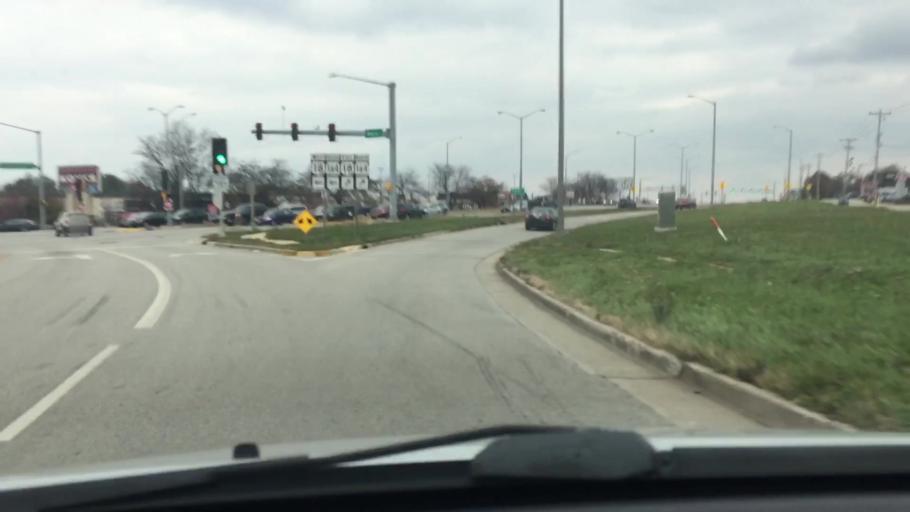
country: US
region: Wisconsin
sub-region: Waukesha County
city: Waukesha
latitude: 43.0267
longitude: -88.1892
